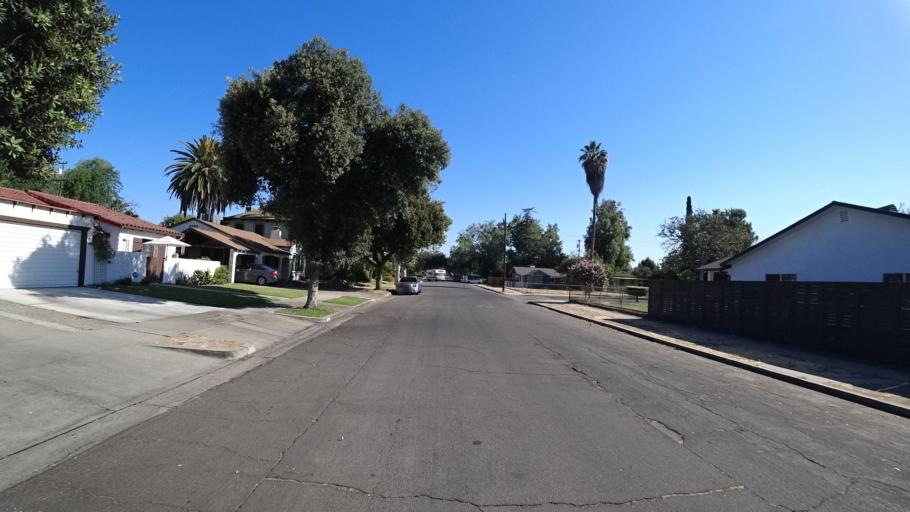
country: US
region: California
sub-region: Fresno County
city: Fresno
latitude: 36.7622
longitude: -119.8097
